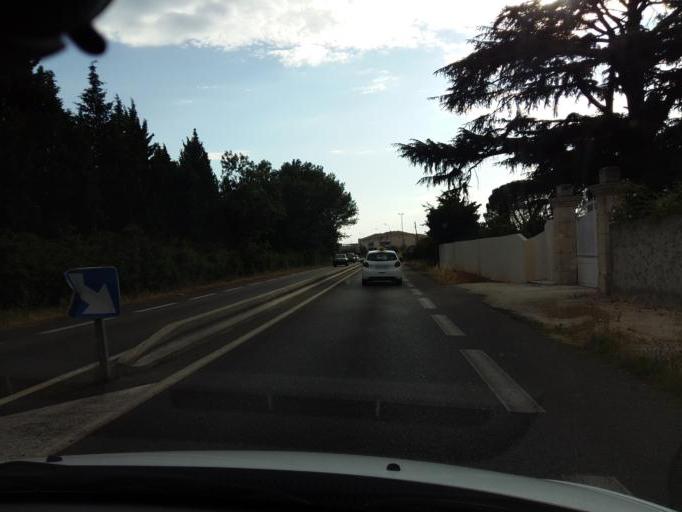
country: FR
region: Provence-Alpes-Cote d'Azur
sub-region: Departement du Vaucluse
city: Le Pontet
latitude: 43.9525
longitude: 4.8656
